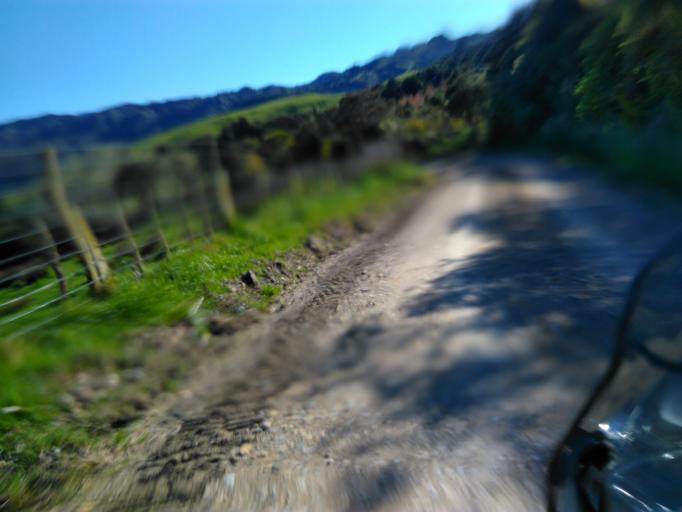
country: NZ
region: Gisborne
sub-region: Gisborne District
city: Gisborne
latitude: -38.3952
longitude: 177.6676
